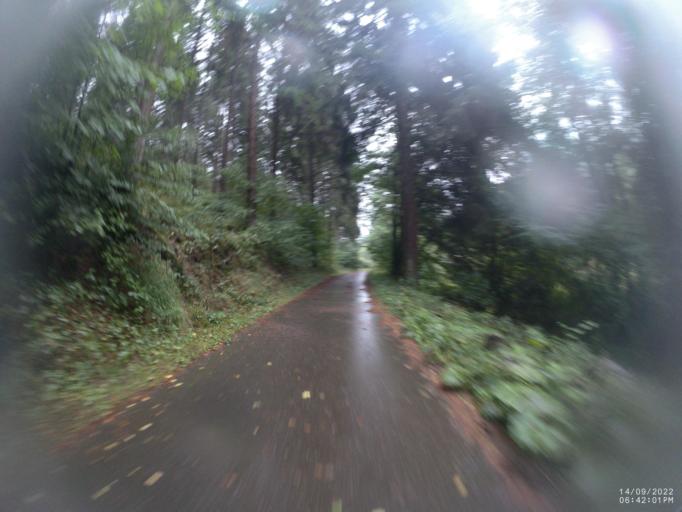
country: DE
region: Rheinland-Pfalz
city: Dorsel
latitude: 50.3653
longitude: 6.7778
